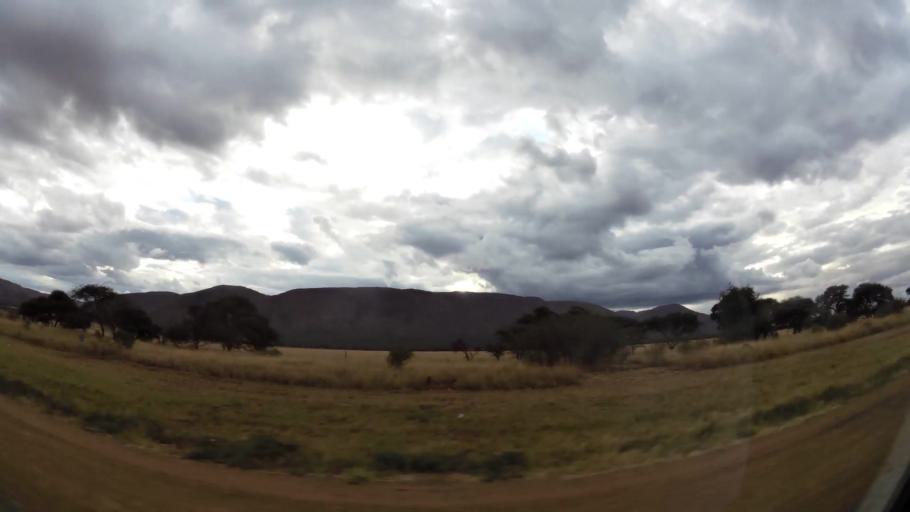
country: ZA
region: Limpopo
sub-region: Waterberg District Municipality
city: Mokopane
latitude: -24.2506
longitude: 28.9904
